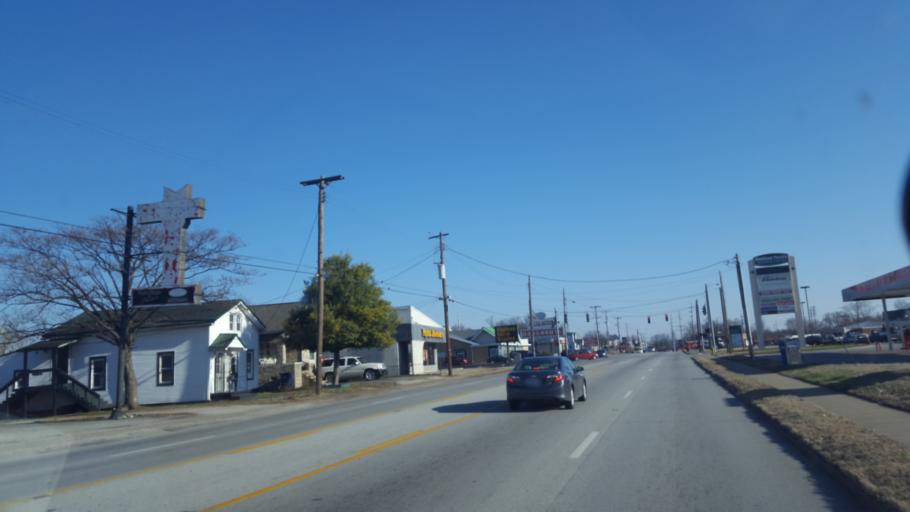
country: US
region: Kentucky
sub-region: Jefferson County
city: Shively
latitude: 38.1930
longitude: -85.8063
